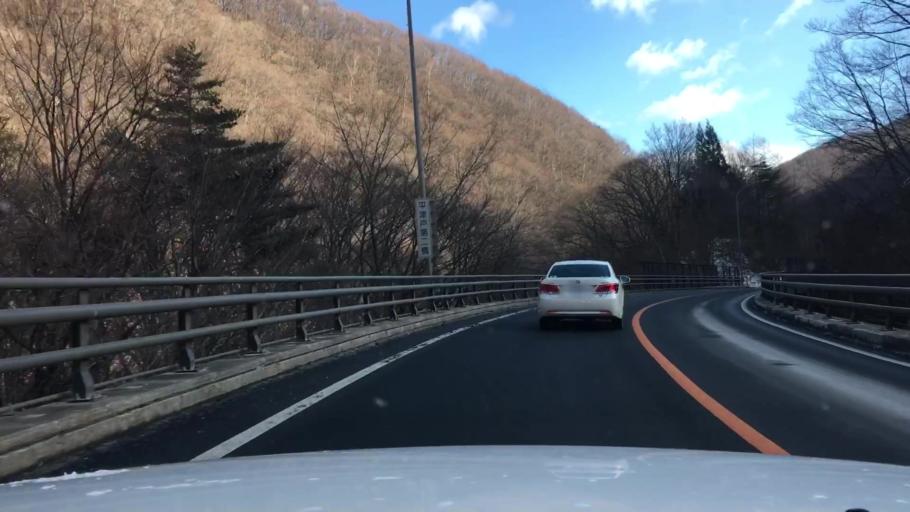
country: JP
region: Iwate
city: Tono
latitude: 39.6216
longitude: 141.5049
